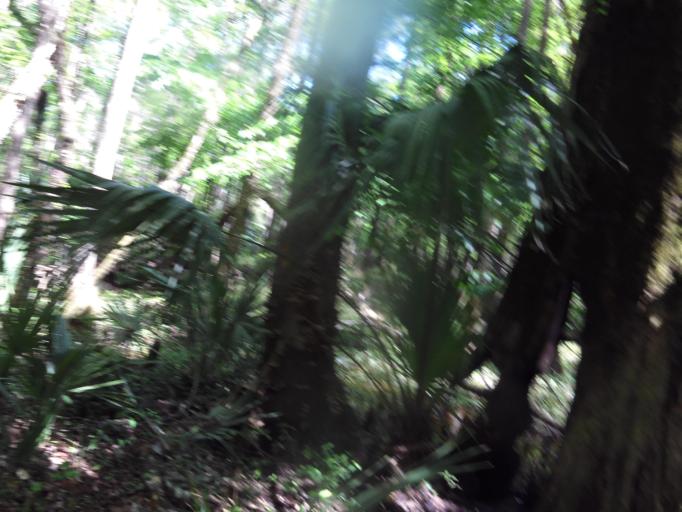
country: US
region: Florida
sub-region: Putnam County
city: Palatka
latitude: 29.6755
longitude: -81.7611
